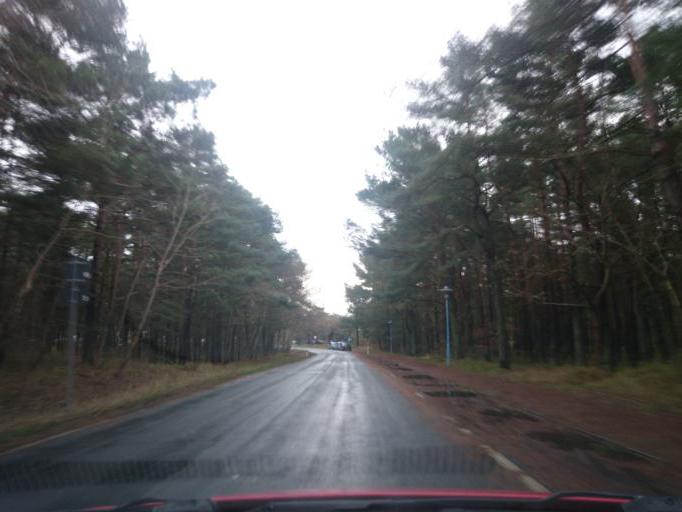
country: DE
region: Mecklenburg-Vorpommern
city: Altenkirchen
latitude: 54.6143
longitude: 13.3768
